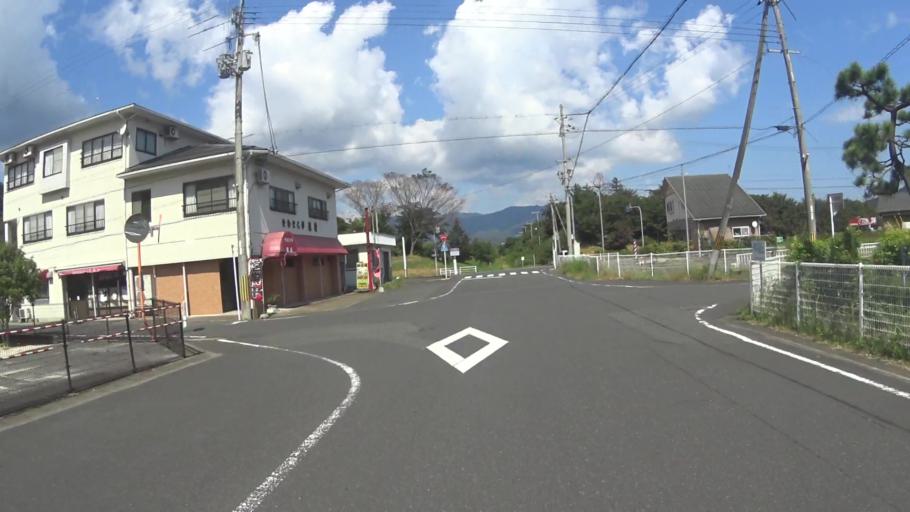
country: JP
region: Kyoto
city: Miyazu
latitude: 35.5519
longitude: 135.1519
